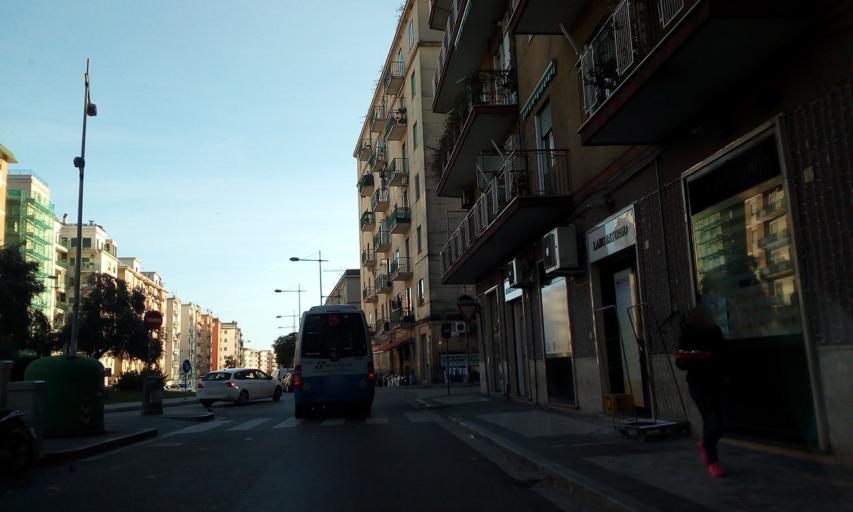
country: IT
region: Campania
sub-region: Provincia di Salerno
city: Capezzano Inferiore
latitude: 40.6817
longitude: 14.7741
